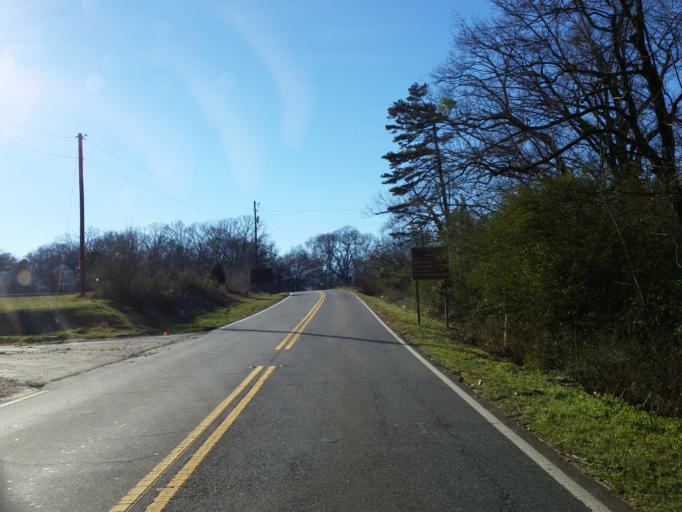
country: US
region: Georgia
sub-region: Cobb County
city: Kennesaw
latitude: 33.9795
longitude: -84.5993
